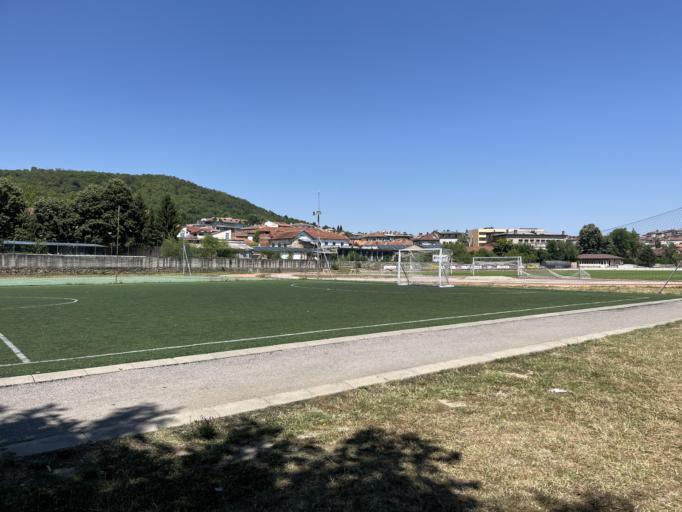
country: BG
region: Gabrovo
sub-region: Obshtina Dryanovo
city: Dryanovo
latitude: 42.9720
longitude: 25.4765
